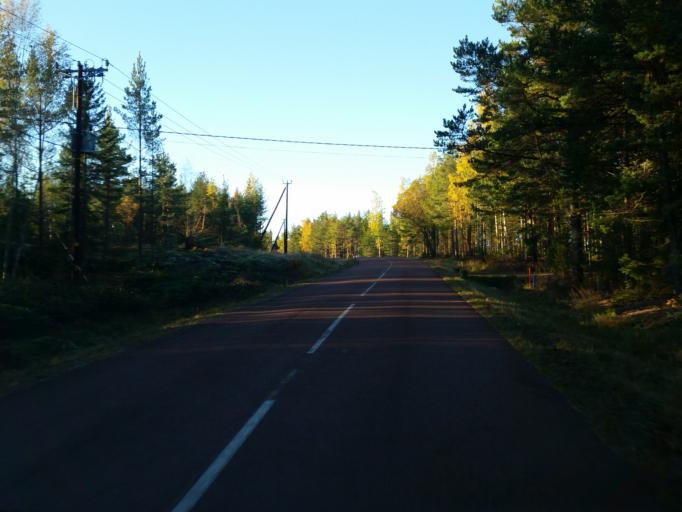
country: AX
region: Alands skaergard
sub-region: Vardoe
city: Vardoe
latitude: 60.2855
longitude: 20.3903
